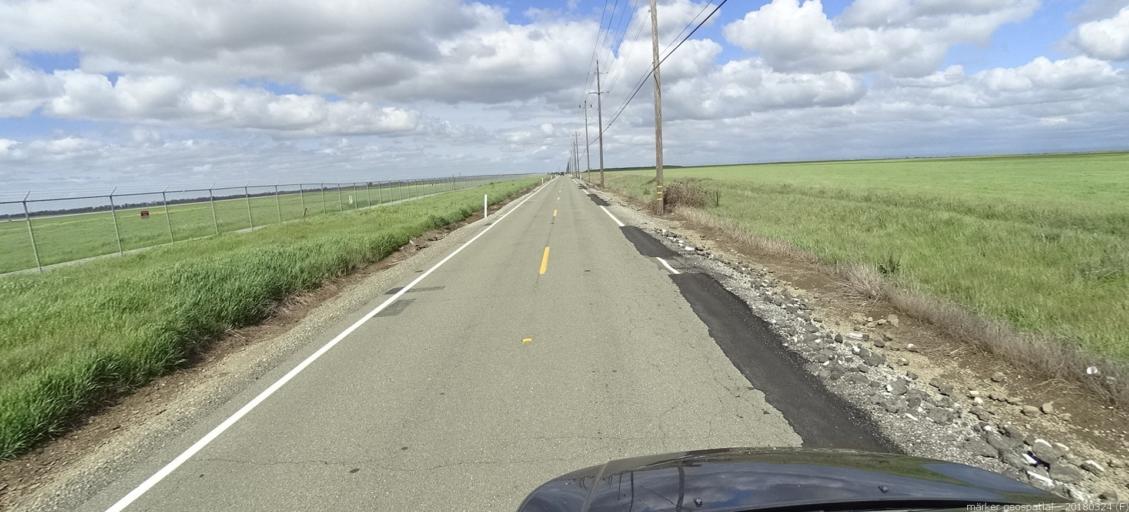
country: US
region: California
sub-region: Sacramento County
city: Elverta
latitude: 38.6960
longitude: -121.5767
